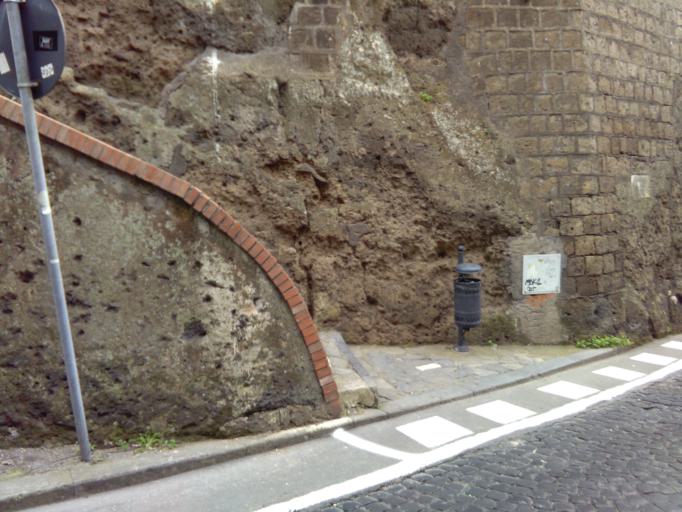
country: IT
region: Campania
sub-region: Provincia di Napoli
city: Sorrento
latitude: 40.6282
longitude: 14.3748
